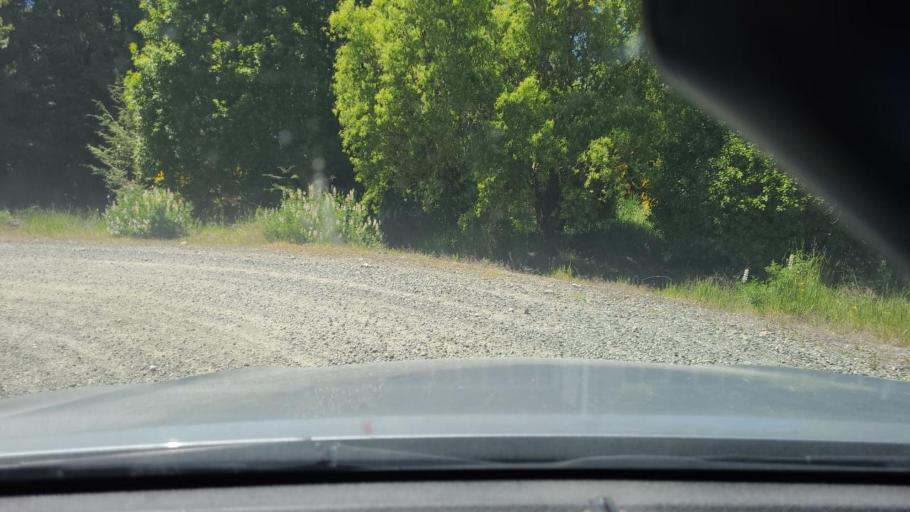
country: NZ
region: Southland
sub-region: Southland District
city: Te Anau
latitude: -45.7766
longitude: 167.6201
